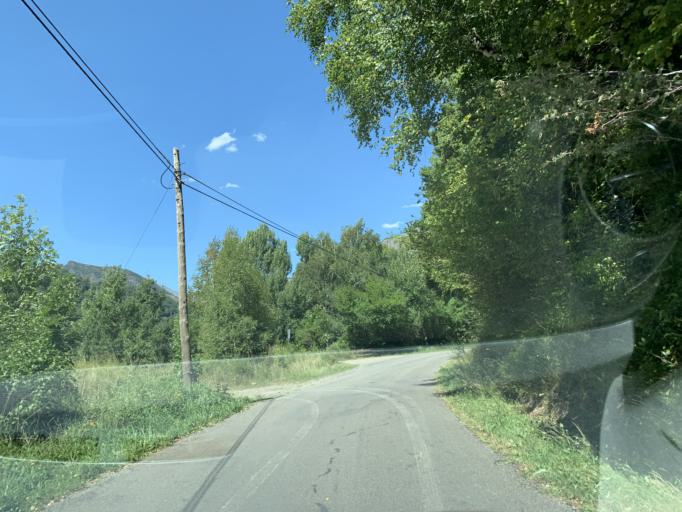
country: ES
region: Aragon
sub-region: Provincia de Huesca
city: Hoz de Jaca
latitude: 42.7125
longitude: -0.3021
